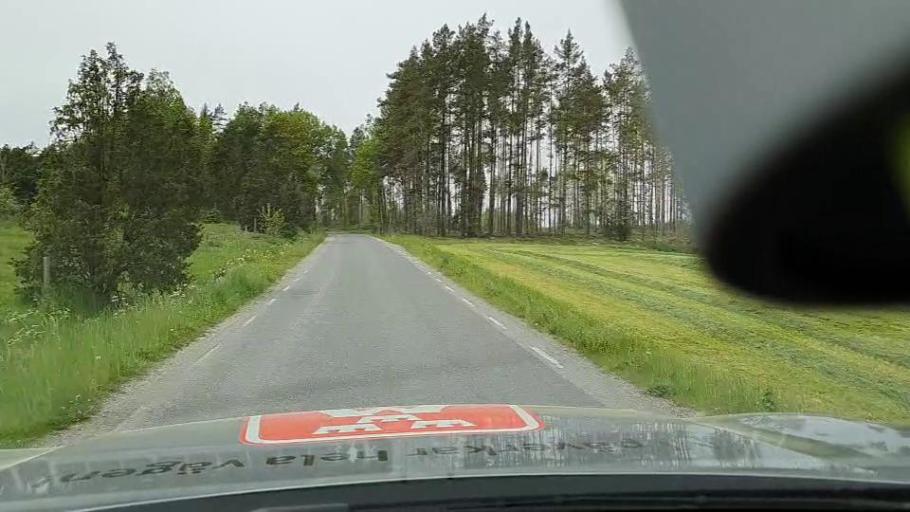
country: SE
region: Soedermanland
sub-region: Flens Kommun
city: Halleforsnas
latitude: 59.1021
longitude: 16.5167
